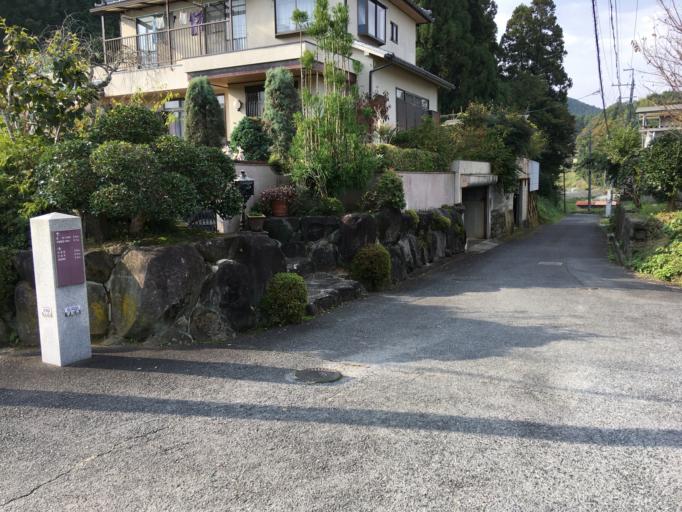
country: JP
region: Nara
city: Haibara-akanedai
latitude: 34.4771
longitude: 135.9259
